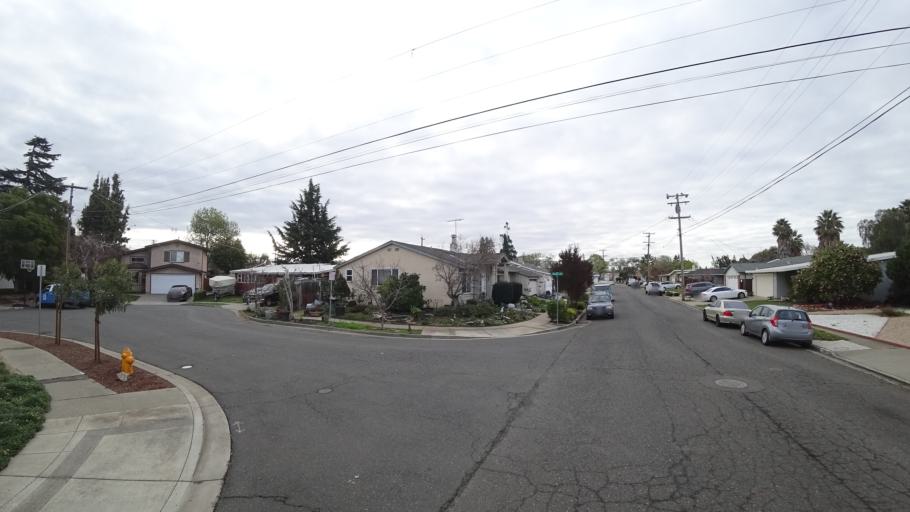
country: US
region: California
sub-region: Alameda County
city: Union City
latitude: 37.6216
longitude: -122.0423
